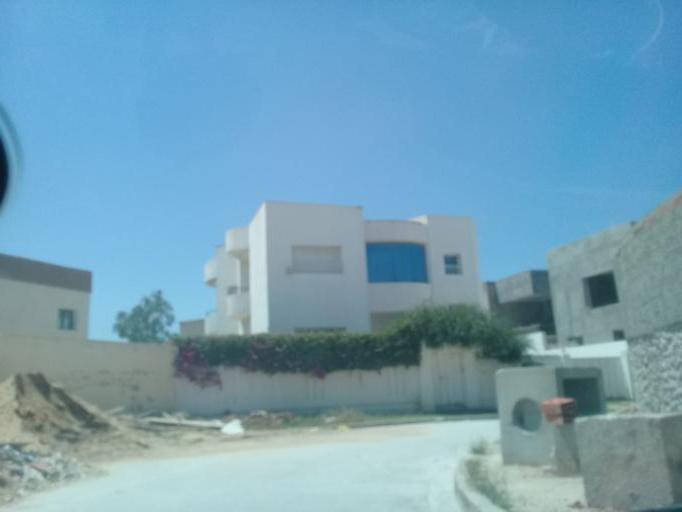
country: TN
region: Tunis
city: La Goulette
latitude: 36.8422
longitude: 10.2677
